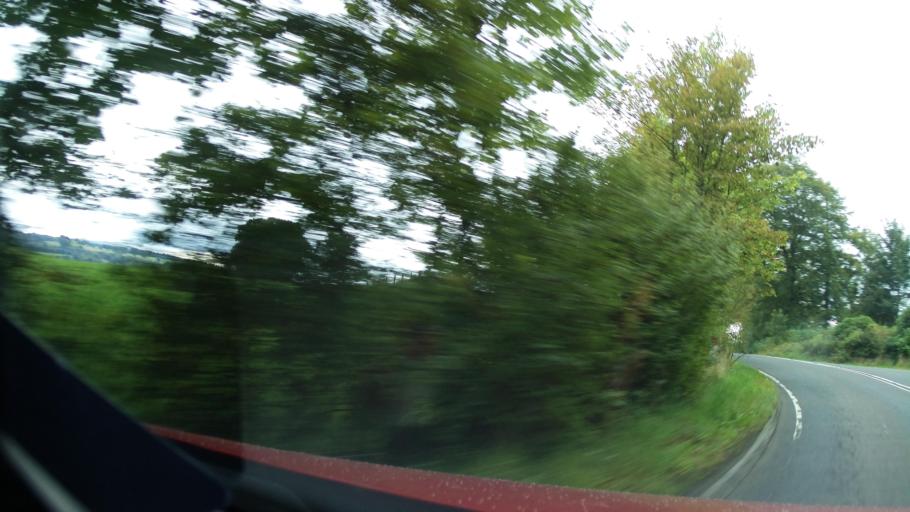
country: GB
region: Scotland
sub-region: Clackmannanshire
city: Dollar
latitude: 56.1759
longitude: -3.6347
